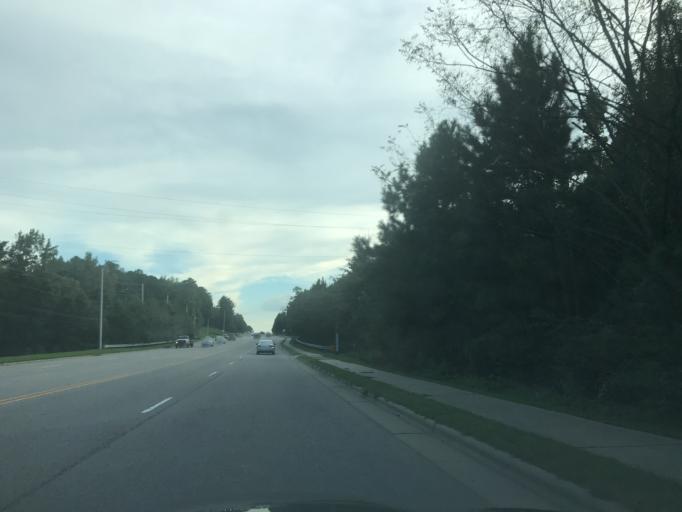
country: US
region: North Carolina
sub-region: Wake County
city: Green Level
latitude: 35.7807
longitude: -78.8720
